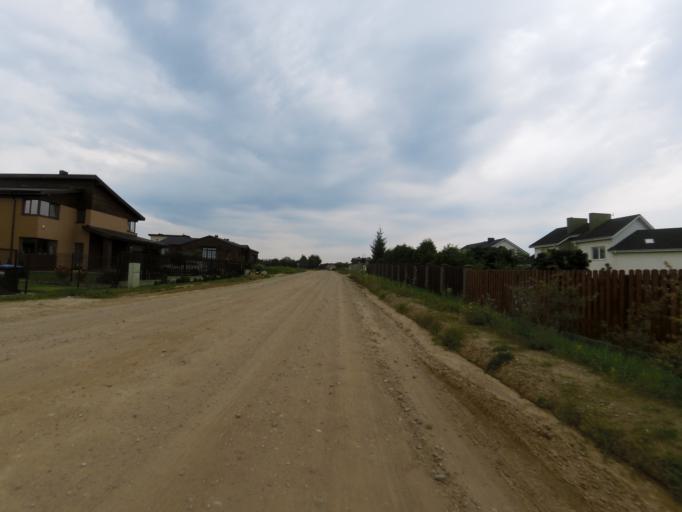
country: LT
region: Vilnius County
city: Pilaite
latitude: 54.7133
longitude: 25.1307
